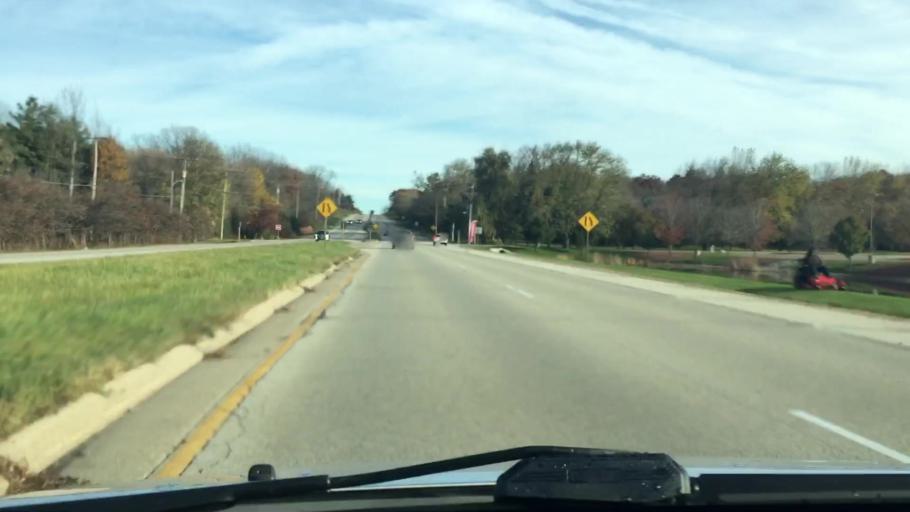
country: US
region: Wisconsin
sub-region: Waukesha County
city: Delafield
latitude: 43.0630
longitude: -88.3679
